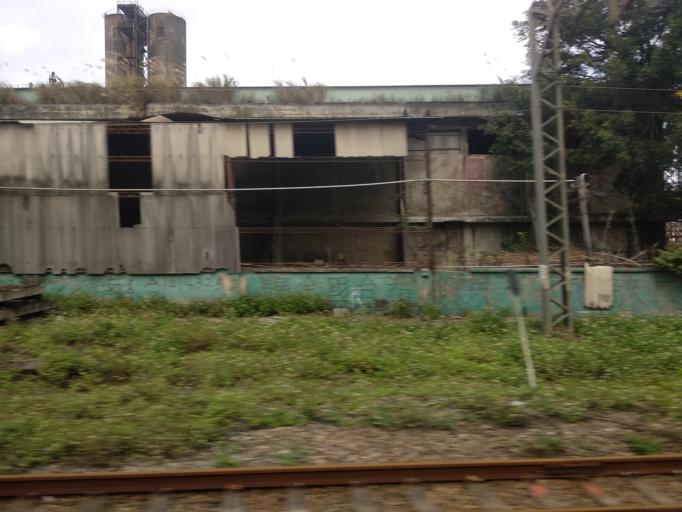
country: TW
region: Taiwan
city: Daxi
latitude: 24.9179
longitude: 121.1817
